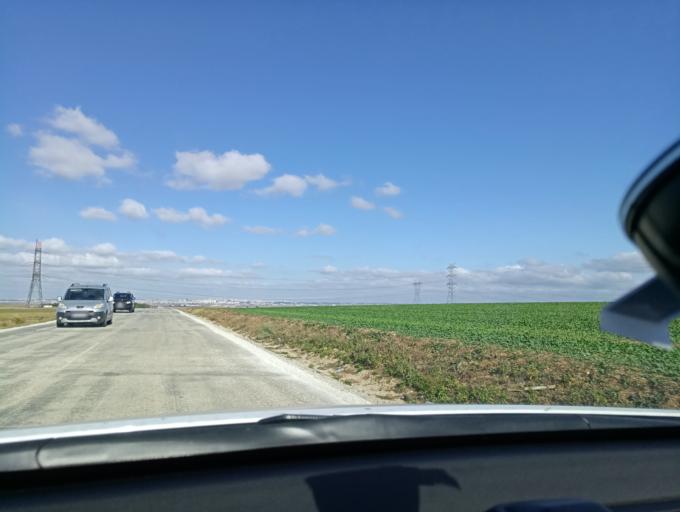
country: TR
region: Tekirdag
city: Corlu
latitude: 41.0566
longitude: 27.8348
